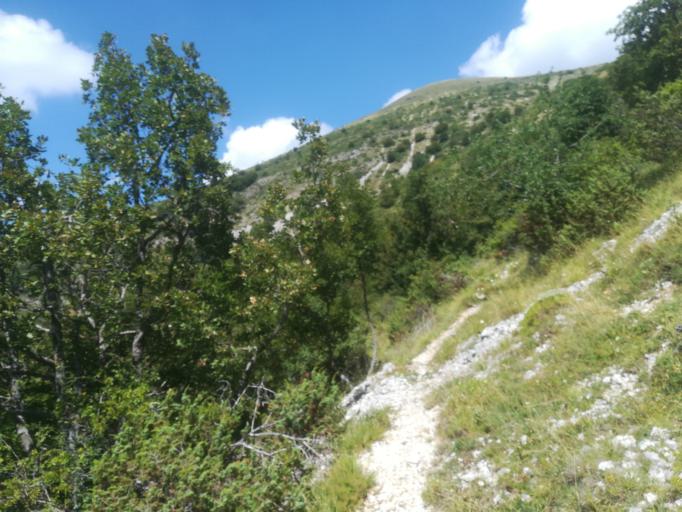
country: IT
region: Umbria
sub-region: Provincia di Perugia
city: Scheggino
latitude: 42.6734
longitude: 12.8580
